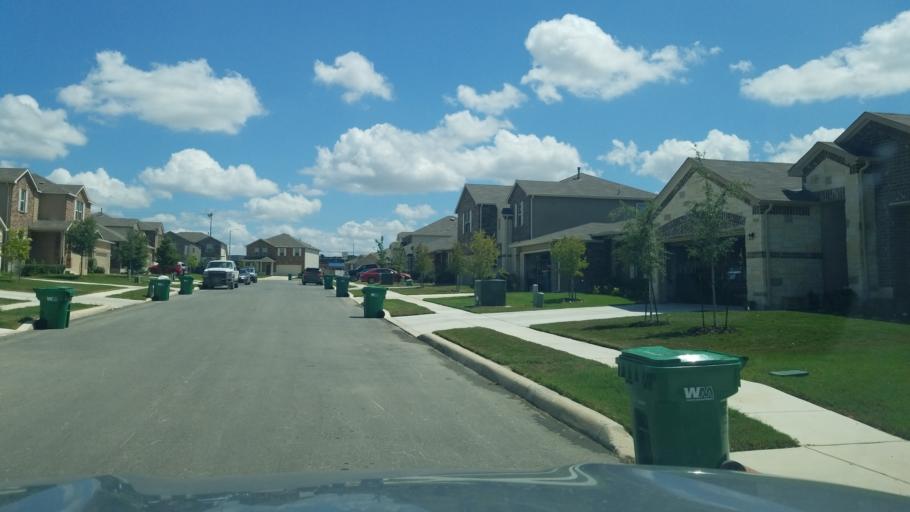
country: US
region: Texas
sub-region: Bexar County
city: Converse
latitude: 29.5341
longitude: -98.3158
